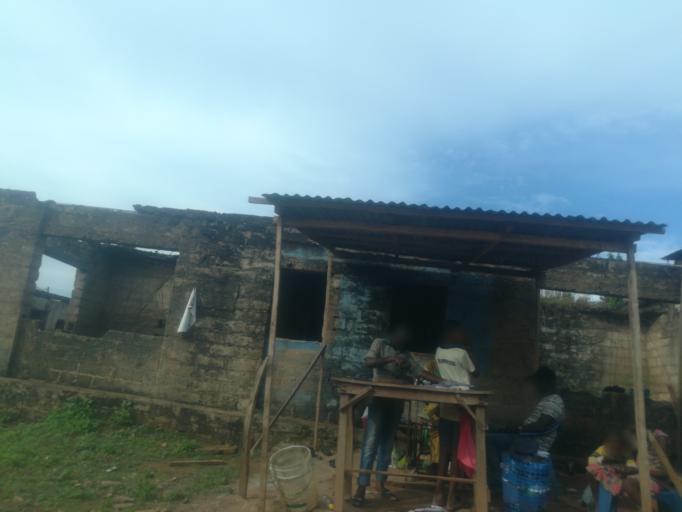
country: NG
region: Oyo
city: Ibadan
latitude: 7.3948
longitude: 3.9398
